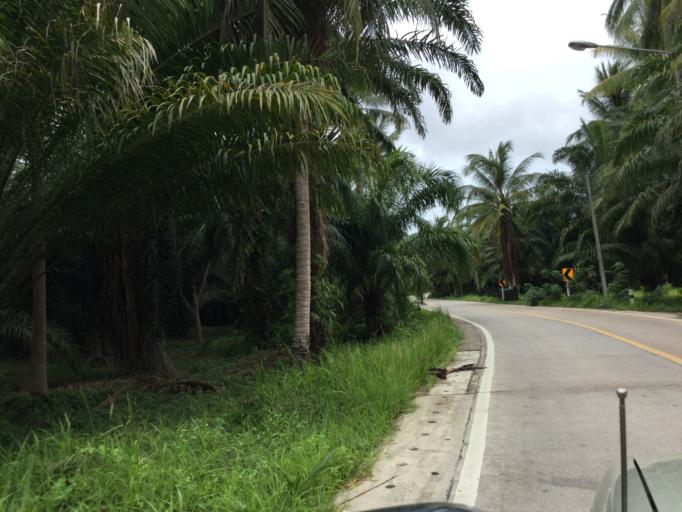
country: TH
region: Surat Thani
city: Ko Pha-Ngan
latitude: 9.7183
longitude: 100.0038
